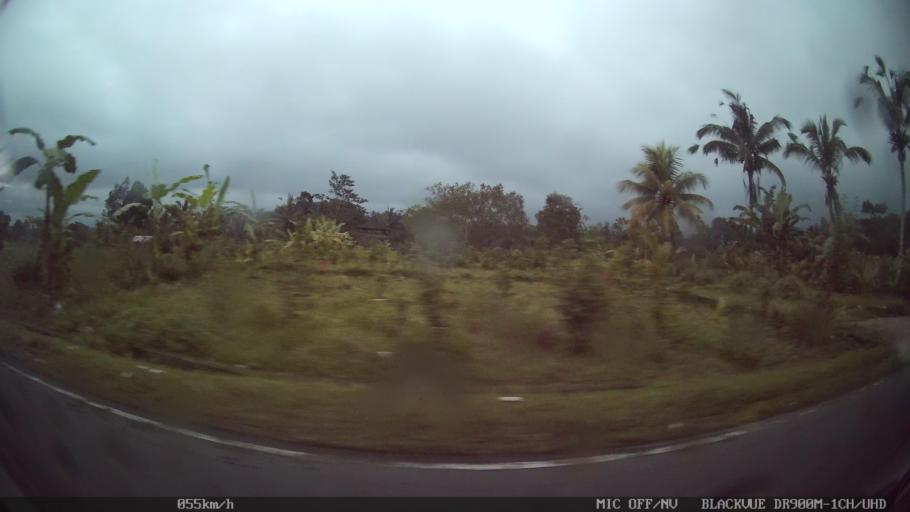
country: ID
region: Bali
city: Banjar Ponggang
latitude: -8.3936
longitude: 115.2556
